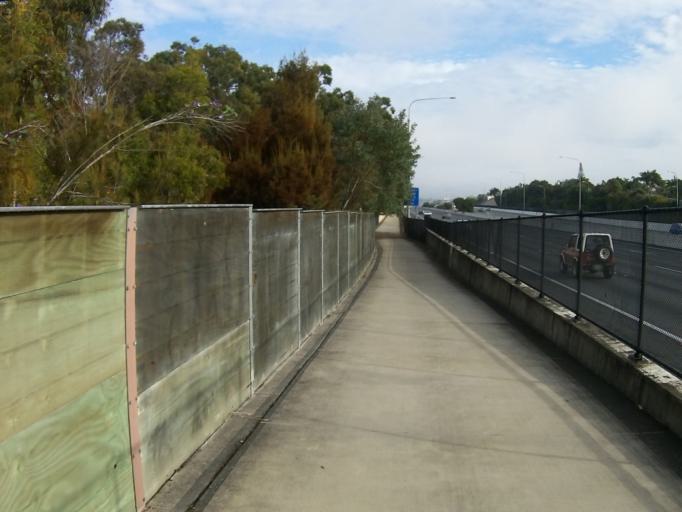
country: AU
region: Queensland
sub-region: Brisbane
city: Upper Mount Gravatt
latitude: -27.5733
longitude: 153.0959
